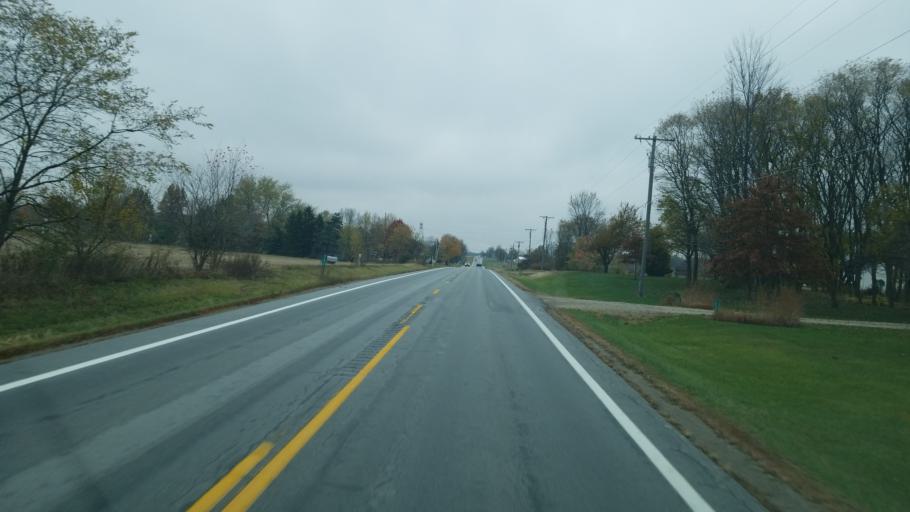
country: US
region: Ohio
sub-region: Union County
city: Marysville
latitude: 40.2867
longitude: -83.3475
